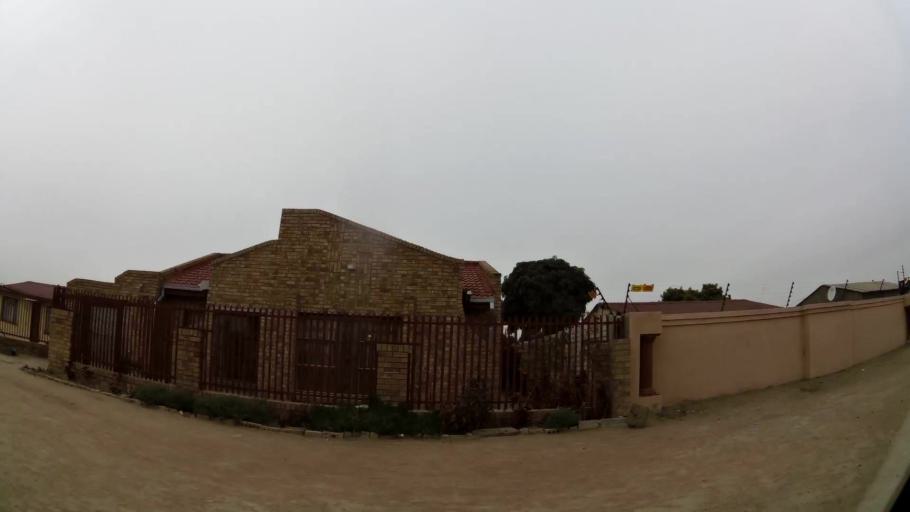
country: ZA
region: Limpopo
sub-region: Capricorn District Municipality
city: Polokwane
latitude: -23.8491
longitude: 29.3936
